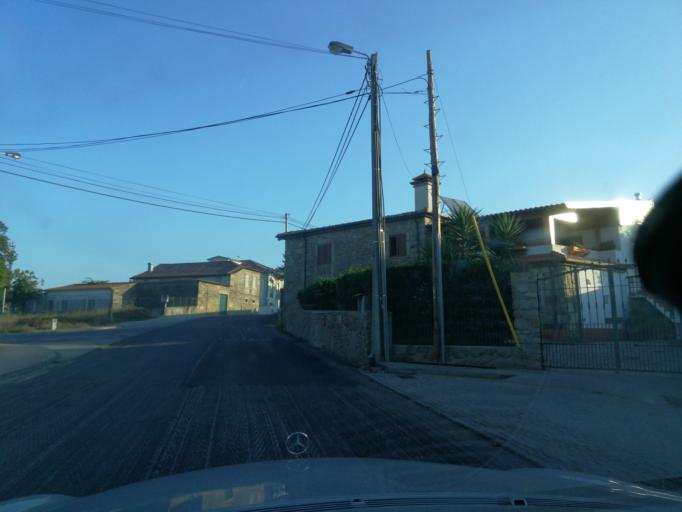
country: PT
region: Braga
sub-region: Braga
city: Braga
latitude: 41.5274
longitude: -8.4279
